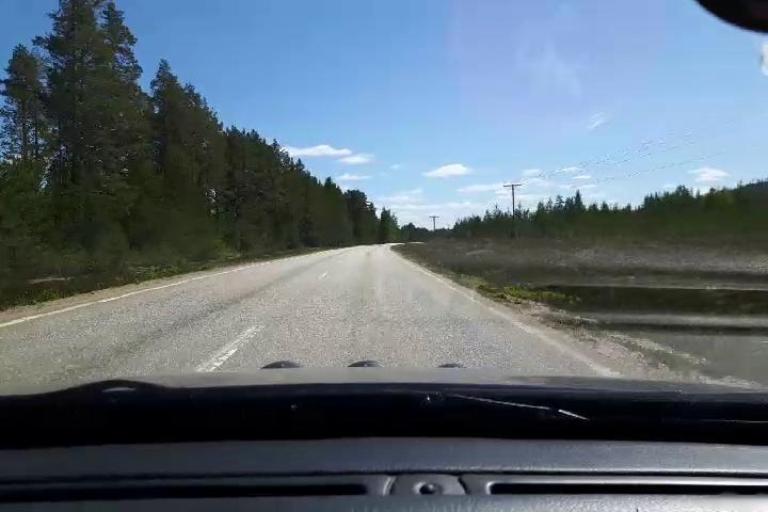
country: SE
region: Jaemtland
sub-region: Harjedalens Kommun
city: Sveg
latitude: 62.1109
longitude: 15.0595
